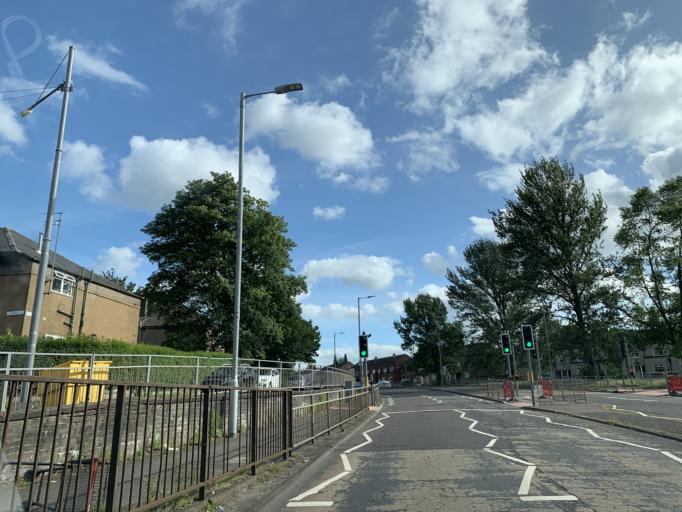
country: GB
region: Scotland
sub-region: Renfrewshire
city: Renfrew
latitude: 55.8549
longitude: -4.3645
